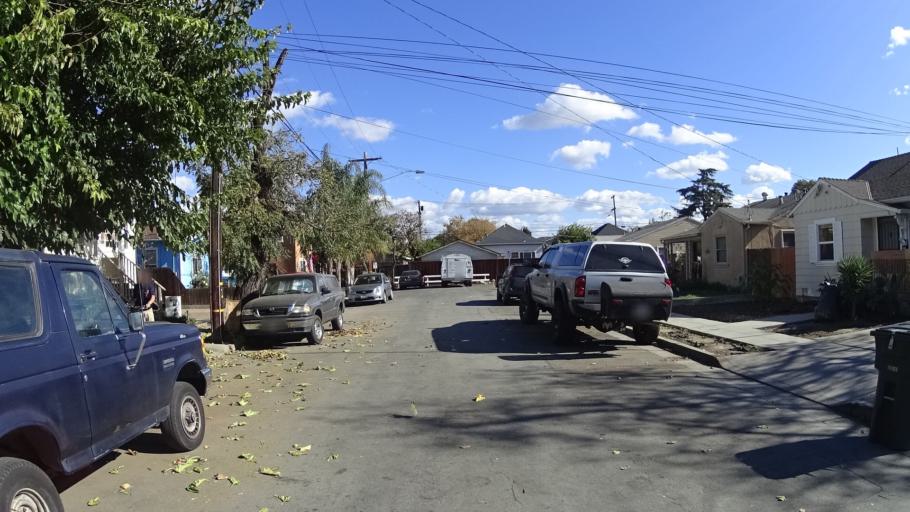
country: US
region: California
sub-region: Santa Clara County
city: Buena Vista
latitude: 37.3272
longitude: -121.9102
